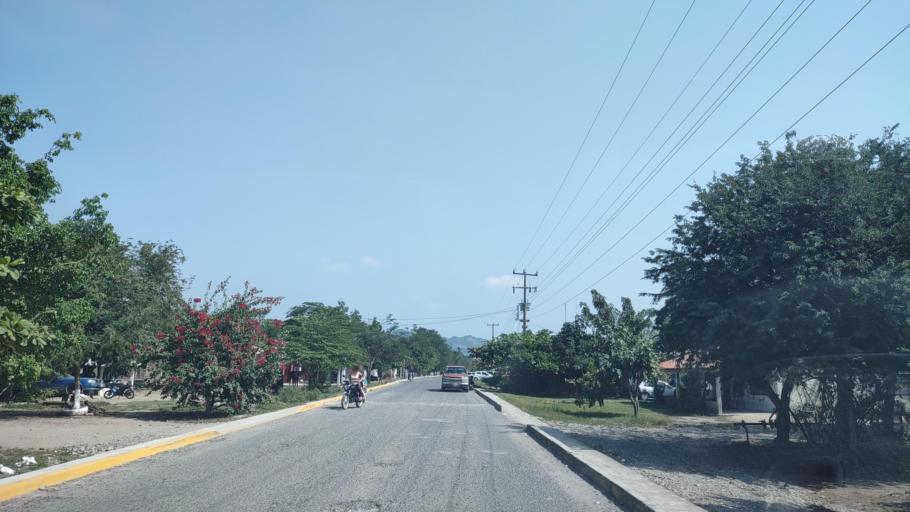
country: MX
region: Puebla
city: Espinal
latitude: 20.2623
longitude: -97.3113
